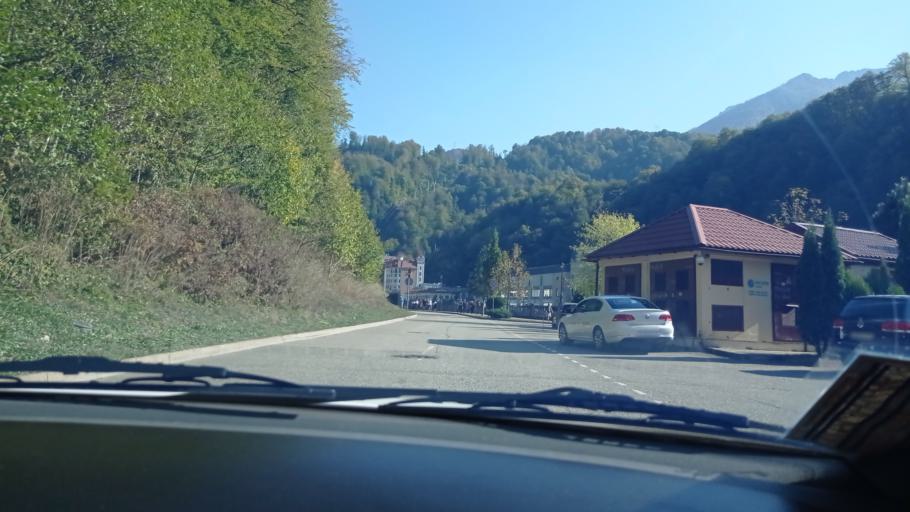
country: RU
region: Krasnodarskiy
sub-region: Sochi City
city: Krasnaya Polyana
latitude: 43.6748
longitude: 40.2894
